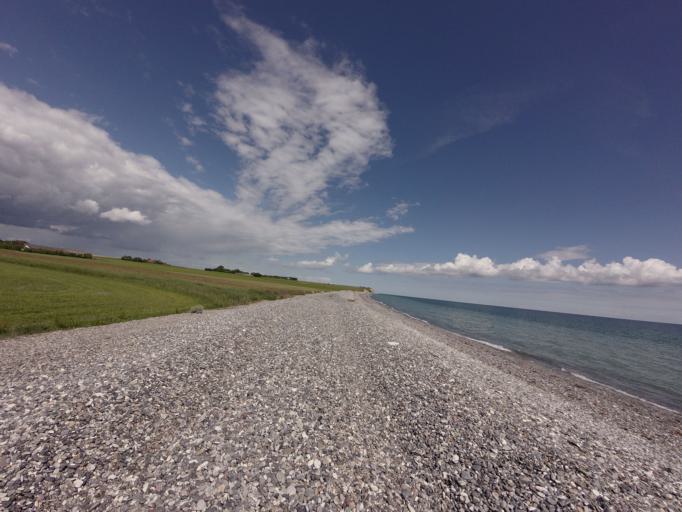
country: DK
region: Central Jutland
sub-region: Norddjurs Kommune
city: Grenaa
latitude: 56.4954
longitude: 10.8705
